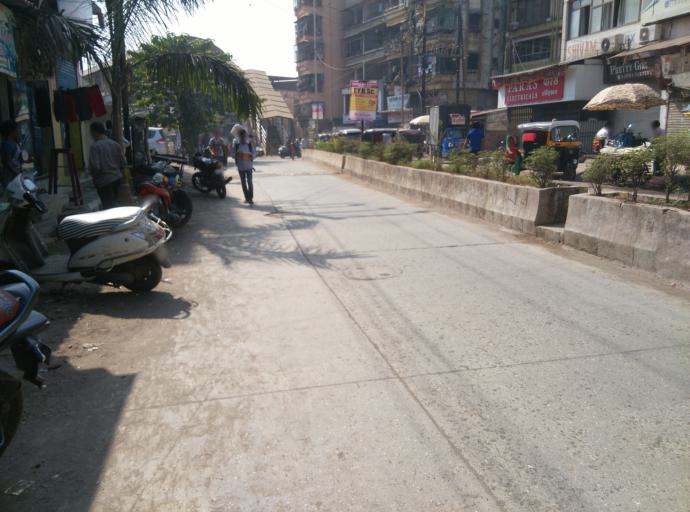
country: IN
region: Maharashtra
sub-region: Thane
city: Ulhasnagar
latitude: 19.2205
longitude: 73.1618
